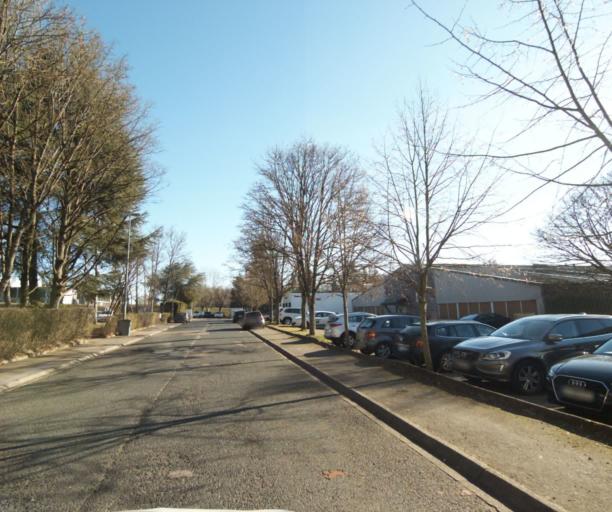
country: FR
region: Lorraine
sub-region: Departement de Meurthe-et-Moselle
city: Laxou
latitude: 48.7030
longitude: 6.1334
